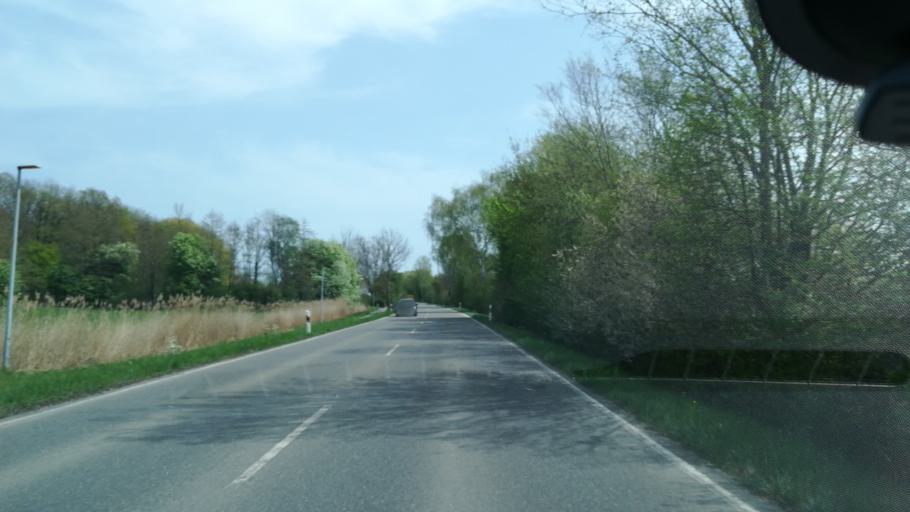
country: DE
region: Baden-Wuerttemberg
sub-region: Freiburg Region
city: Moos
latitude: 47.7496
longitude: 8.9471
